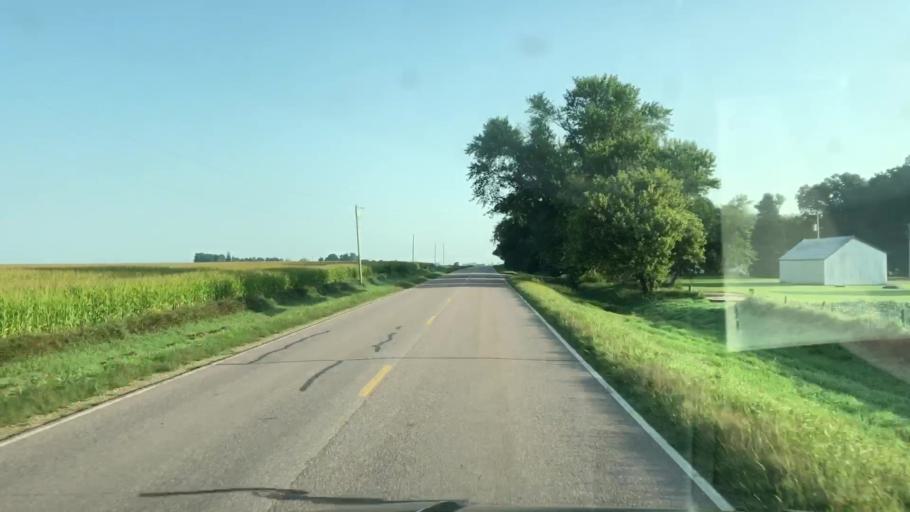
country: US
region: Iowa
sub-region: Sioux County
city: Hull
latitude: 43.2052
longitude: -96.0006
